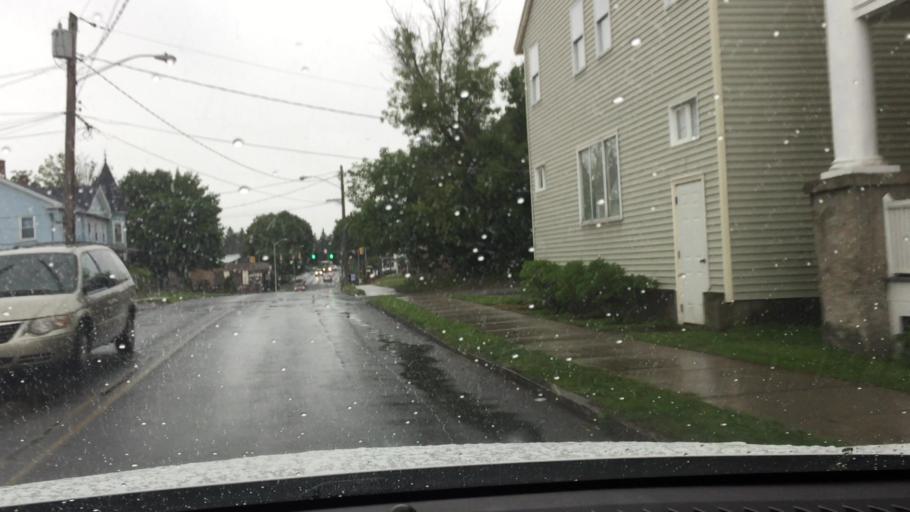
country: US
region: Massachusetts
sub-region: Berkshire County
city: Pittsfield
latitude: 42.4560
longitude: -73.2556
